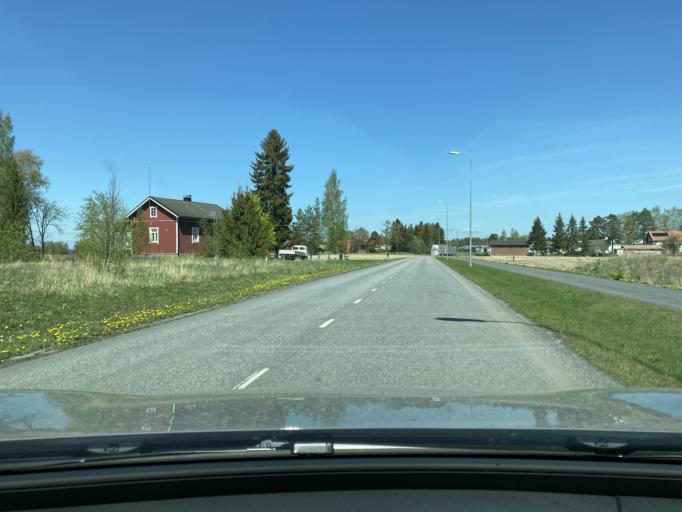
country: FI
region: Pirkanmaa
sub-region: Lounais-Pirkanmaa
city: Vammala
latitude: 61.3229
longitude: 22.9153
